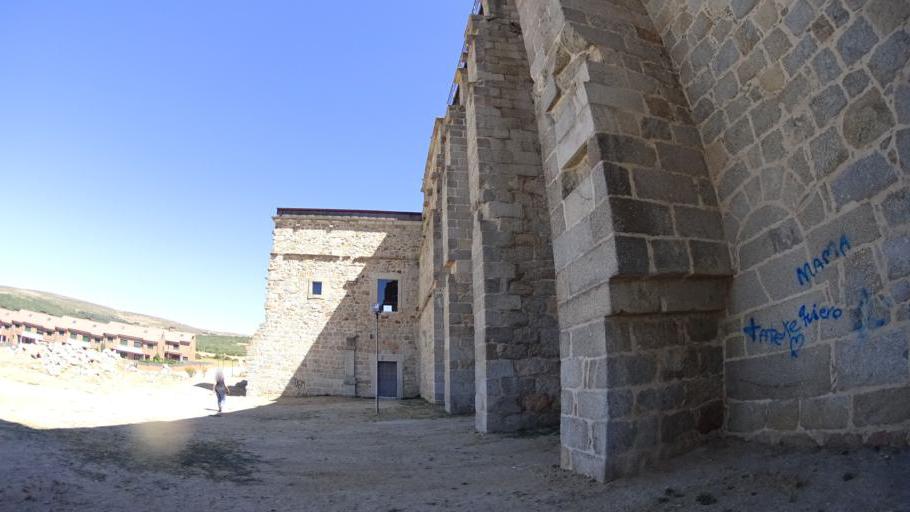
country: ES
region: Castille and Leon
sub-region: Provincia de Avila
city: Las Navas del Marques
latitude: 40.6057
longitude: -4.3267
